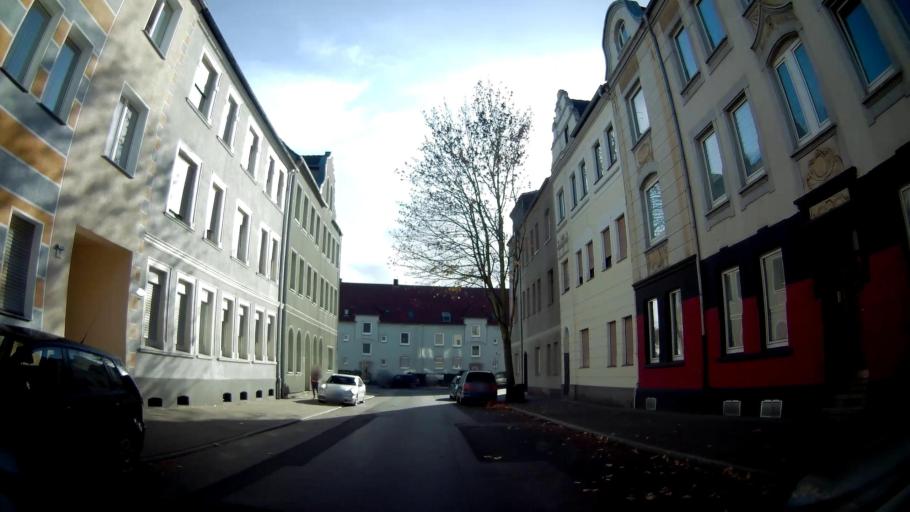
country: DE
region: North Rhine-Westphalia
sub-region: Regierungsbezirk Munster
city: Gladbeck
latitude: 51.5560
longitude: 7.0054
